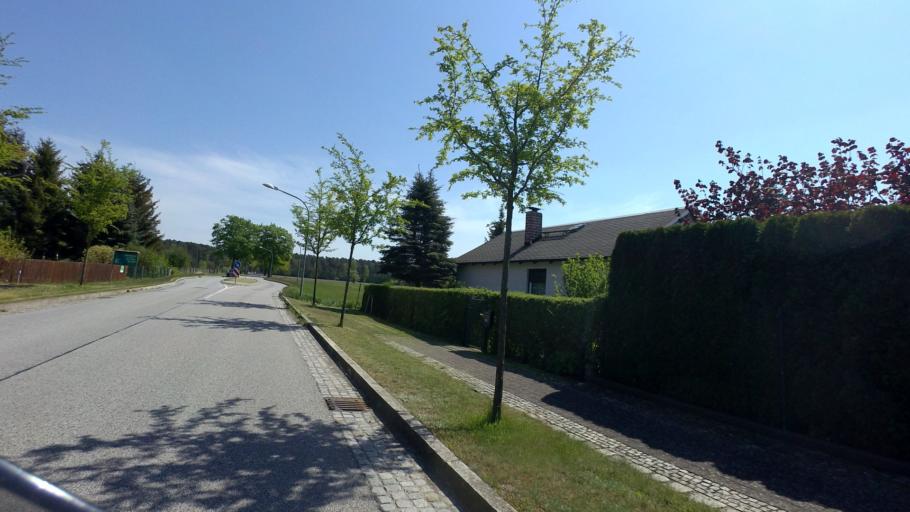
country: DE
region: Brandenburg
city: Halbe
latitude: 52.1082
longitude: 13.7706
